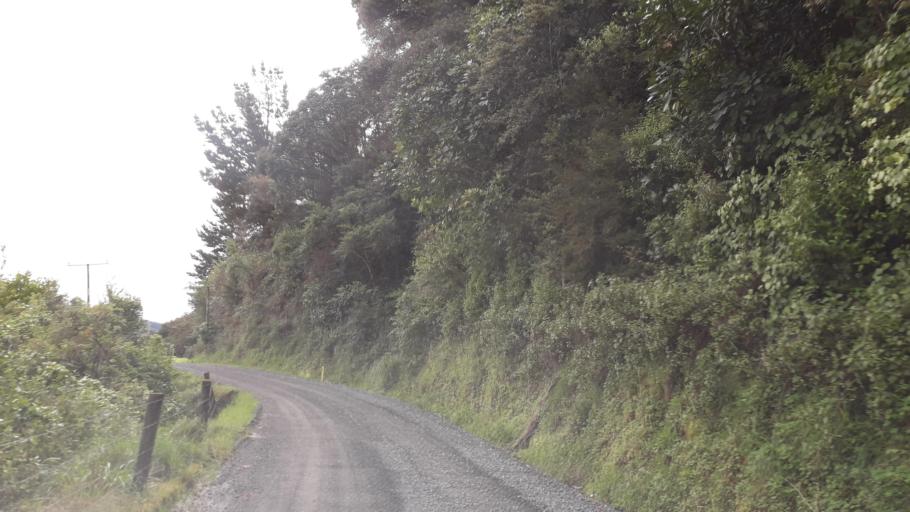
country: NZ
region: Northland
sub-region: Far North District
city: Taipa
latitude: -35.0974
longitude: 173.5409
